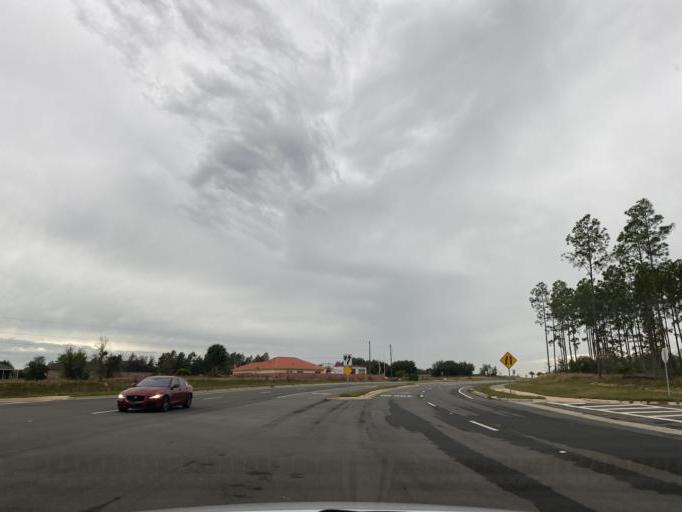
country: US
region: Florida
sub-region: Orange County
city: Oakland
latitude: 28.5399
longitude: -81.6853
